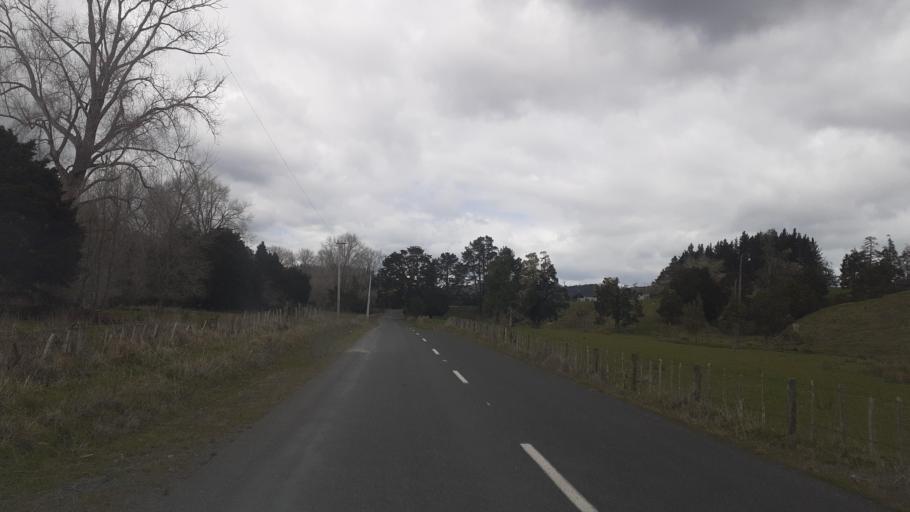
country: NZ
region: Northland
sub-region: Far North District
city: Moerewa
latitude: -35.5805
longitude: 173.9708
